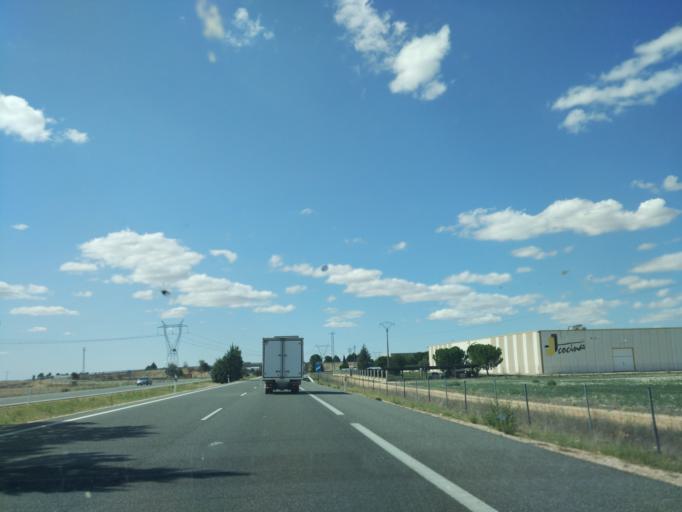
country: ES
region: Castille and Leon
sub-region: Provincia de Valladolid
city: San Vicente del Palacio
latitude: 41.2340
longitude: -4.8561
